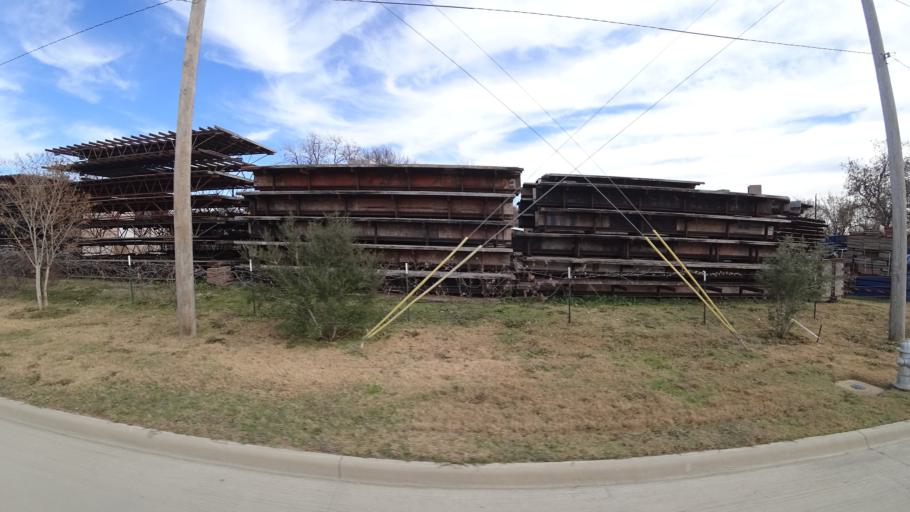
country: US
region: Texas
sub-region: Denton County
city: Lewisville
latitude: 33.0328
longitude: -96.9777
